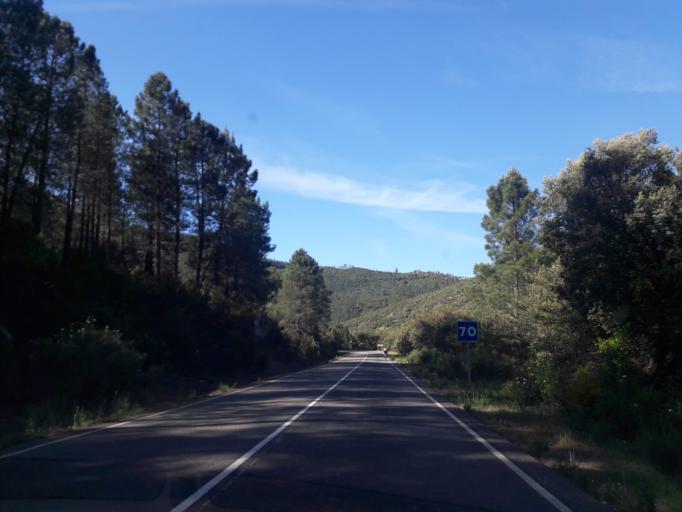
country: ES
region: Castille and Leon
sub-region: Provincia de Salamanca
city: Sotoserrano
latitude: 40.4133
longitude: -6.0527
